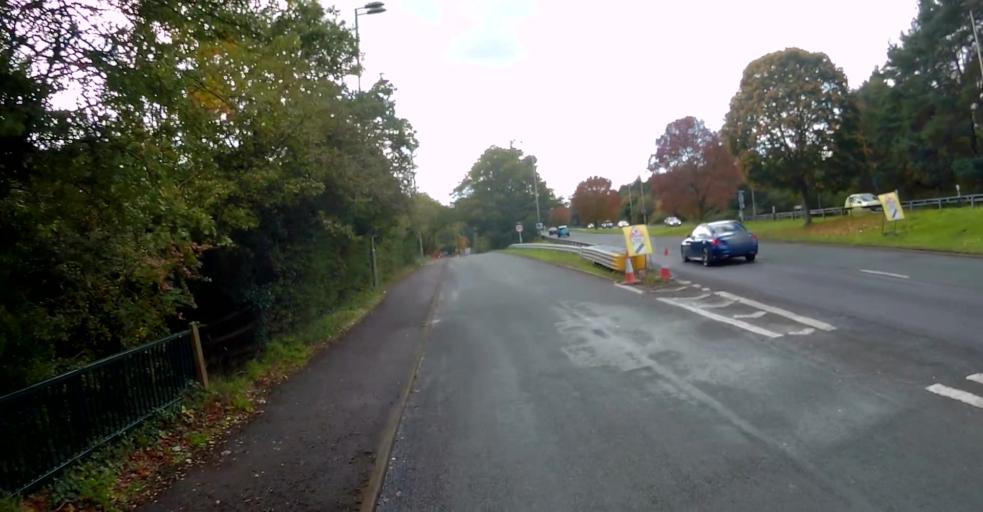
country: GB
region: England
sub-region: Hampshire
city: Aldershot
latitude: 51.2632
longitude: -0.7653
